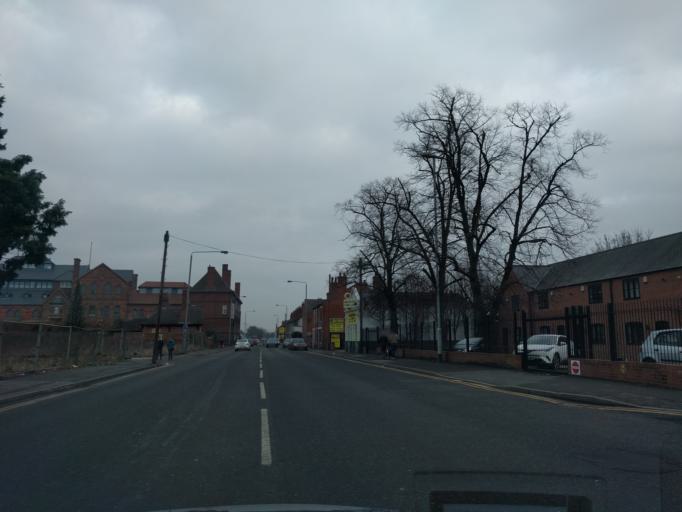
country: GB
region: England
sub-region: Nottinghamshire
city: Newark on Trent
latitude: 53.0810
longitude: -0.8060
